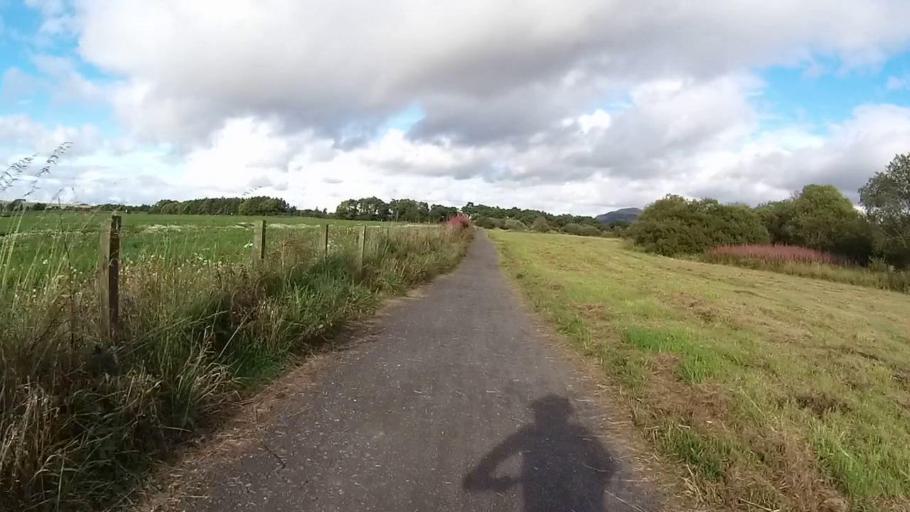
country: GB
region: Scotland
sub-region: Perth and Kinross
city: Milnathort
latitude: 56.2177
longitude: -3.4027
